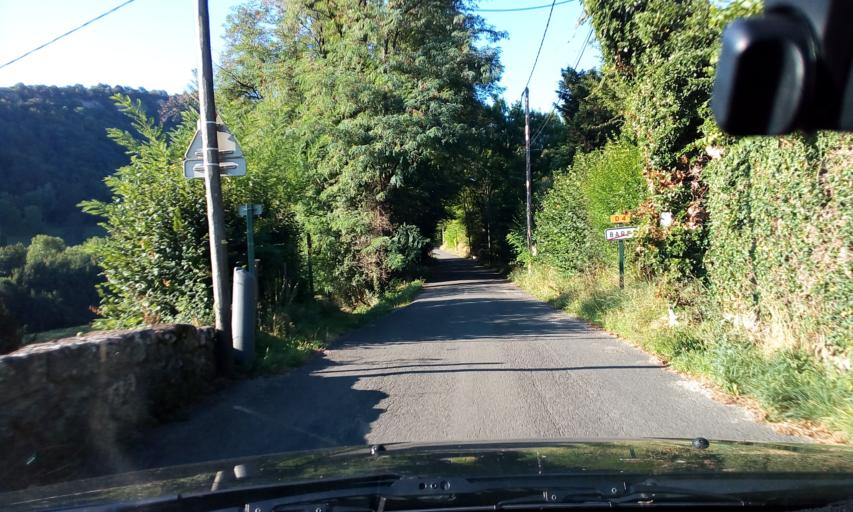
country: FR
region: Rhone-Alpes
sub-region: Departement de la Savoie
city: Barberaz
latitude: 45.5466
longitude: 5.9365
